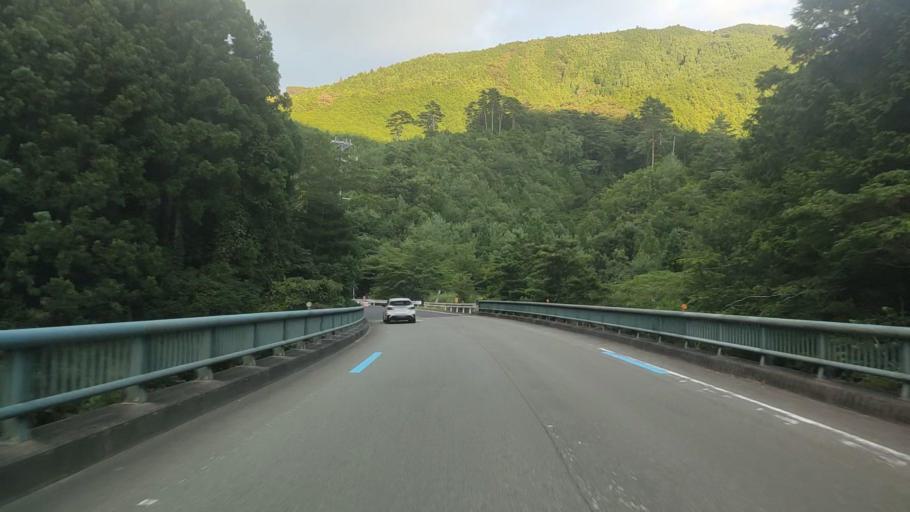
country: JP
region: Wakayama
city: Tanabe
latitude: 33.8301
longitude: 135.6482
